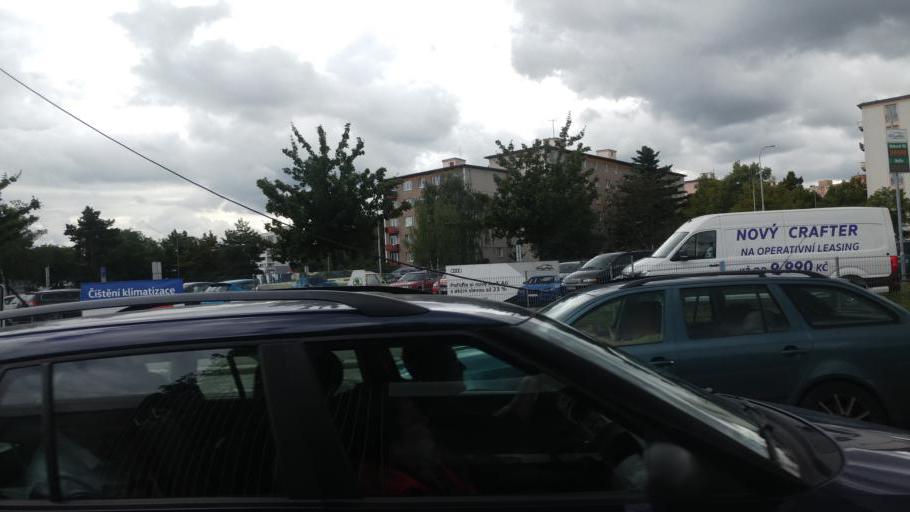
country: CZ
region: Praha
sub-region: Praha 9
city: Prosek
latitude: 50.0916
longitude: 14.4987
